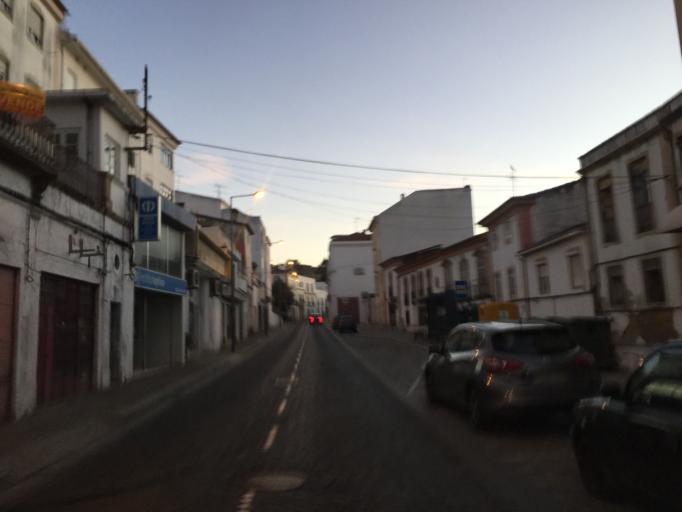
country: PT
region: Portalegre
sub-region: Portalegre
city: Portalegre
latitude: 39.2952
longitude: -7.4308
